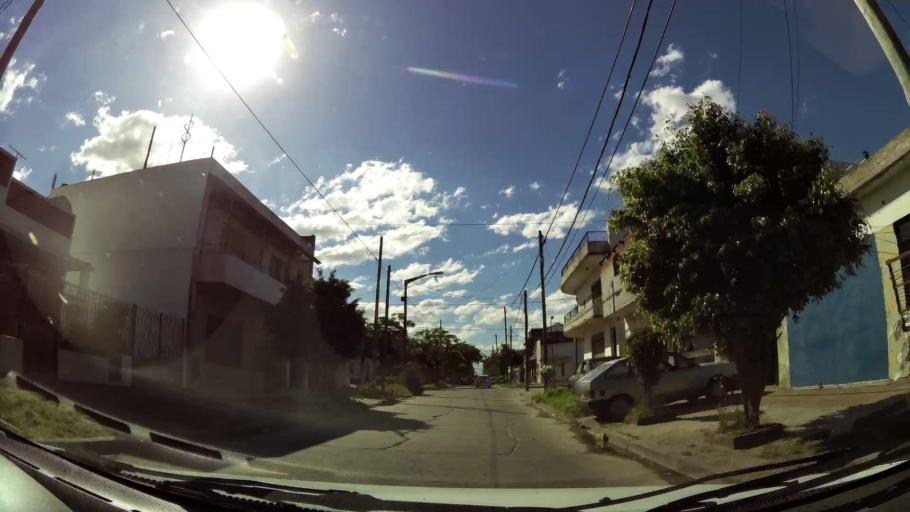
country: AR
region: Buenos Aires
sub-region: Partido de General San Martin
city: General San Martin
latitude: -34.5254
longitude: -58.5768
